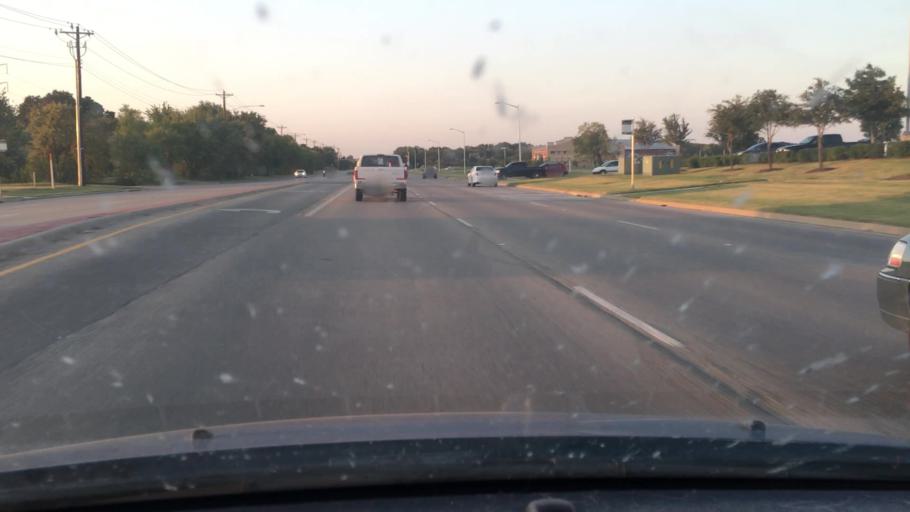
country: US
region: Texas
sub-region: Denton County
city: Denton
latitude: 33.2001
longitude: -97.0911
